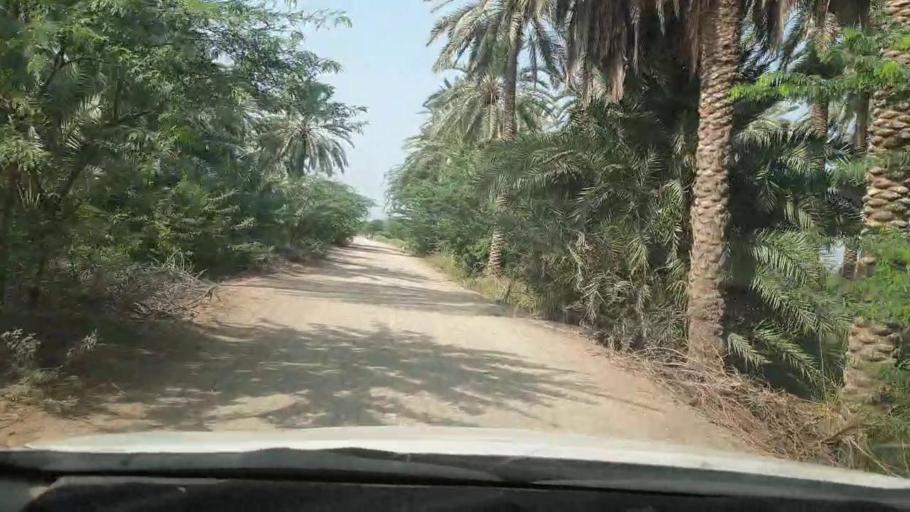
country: PK
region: Sindh
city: Rohri
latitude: 27.6003
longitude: 68.8704
